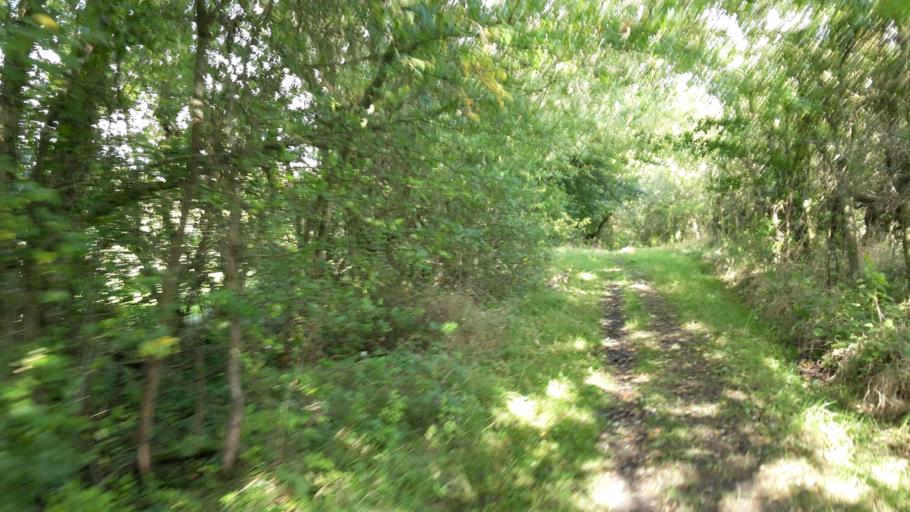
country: GB
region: Scotland
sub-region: South Lanarkshire
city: Law
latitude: 55.7271
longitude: -3.8658
